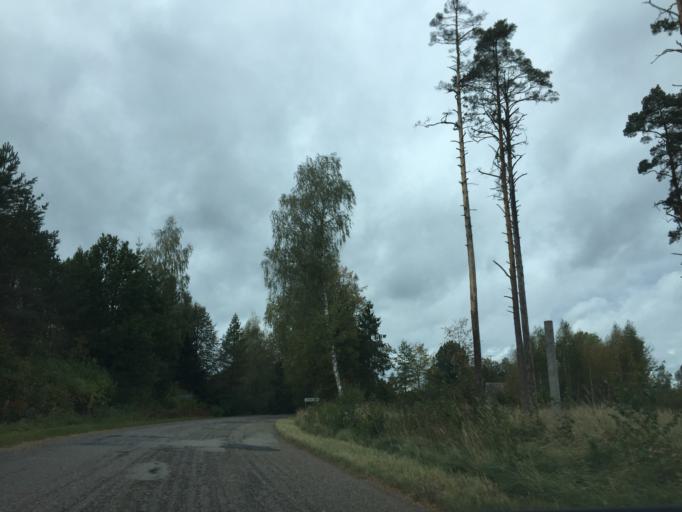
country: LV
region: Olaine
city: Olaine
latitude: 56.7655
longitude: 23.8845
